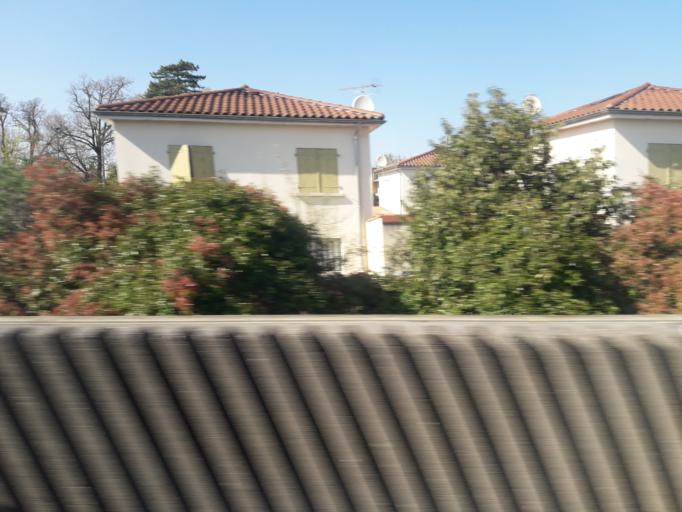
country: FR
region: Rhone-Alpes
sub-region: Departement de la Drome
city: Romans-sur-Isere
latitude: 45.0486
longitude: 5.0666
